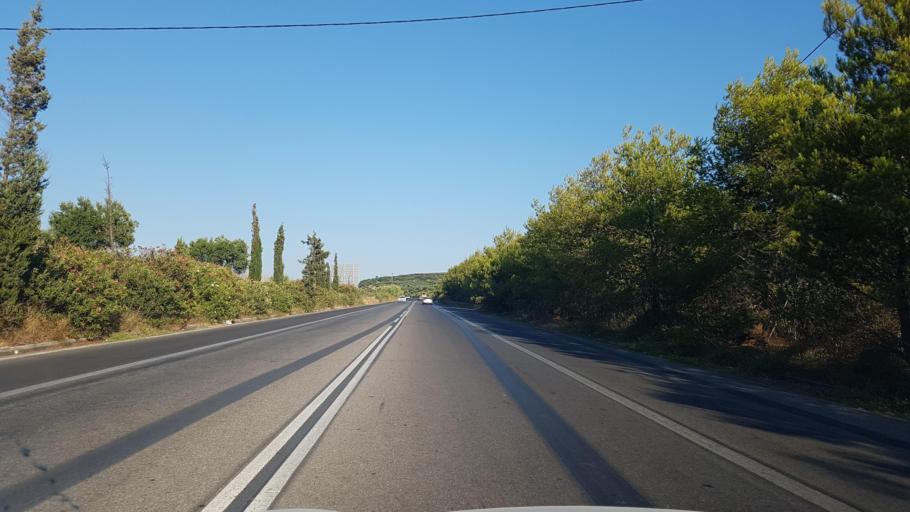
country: GR
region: Crete
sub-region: Nomos Chanias
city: Kolympari
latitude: 35.5268
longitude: 23.7978
